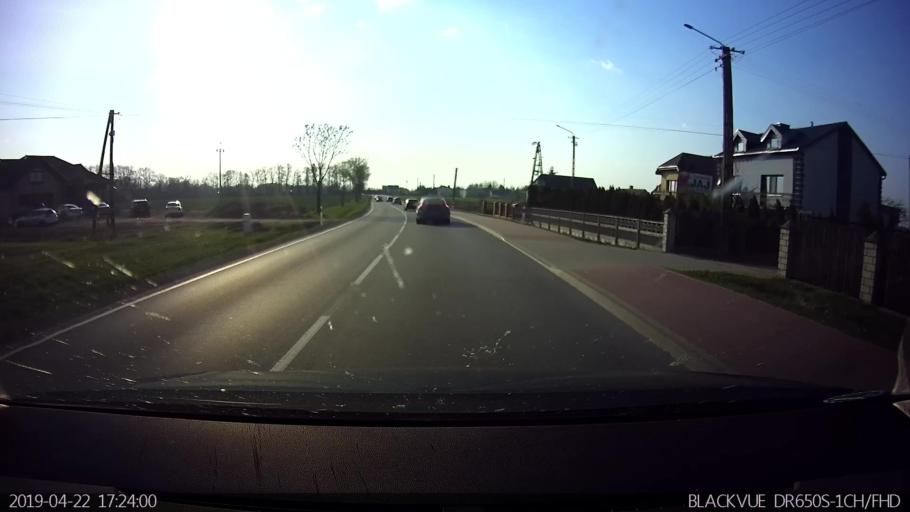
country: PL
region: Masovian Voivodeship
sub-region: Powiat sokolowski
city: Sokolow Podlaski
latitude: 52.3938
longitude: 22.3096
